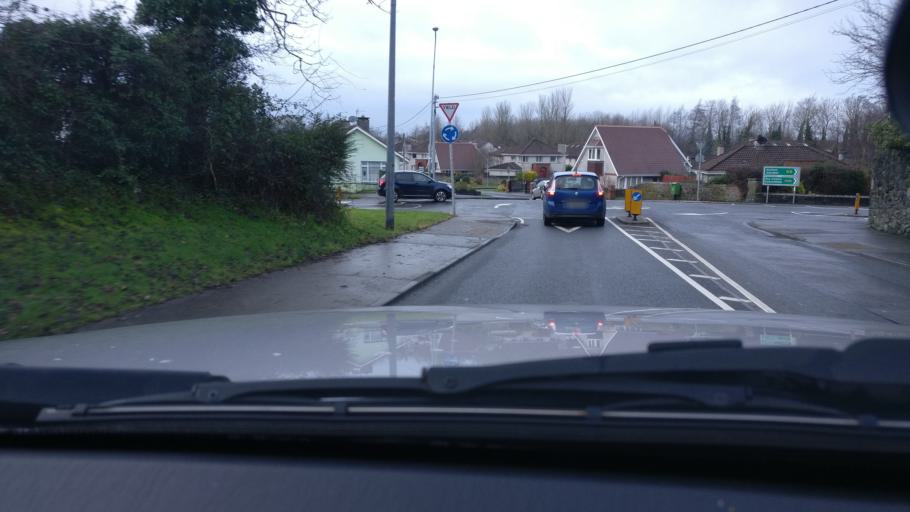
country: IE
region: Leinster
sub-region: An Iarmhi
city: Athlone
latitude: 53.4310
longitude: -7.9272
